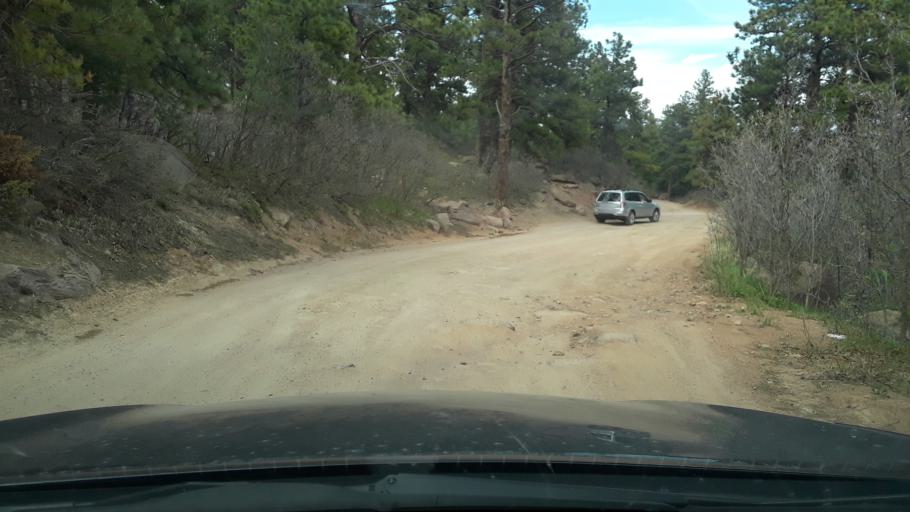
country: US
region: Colorado
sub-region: El Paso County
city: Palmer Lake
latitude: 39.0741
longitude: -104.9177
